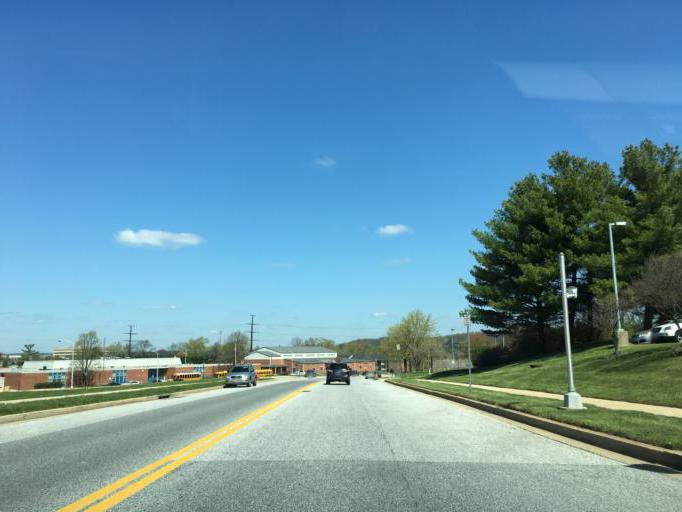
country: US
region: Maryland
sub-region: Baltimore County
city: Timonium
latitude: 39.4601
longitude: -76.6300
